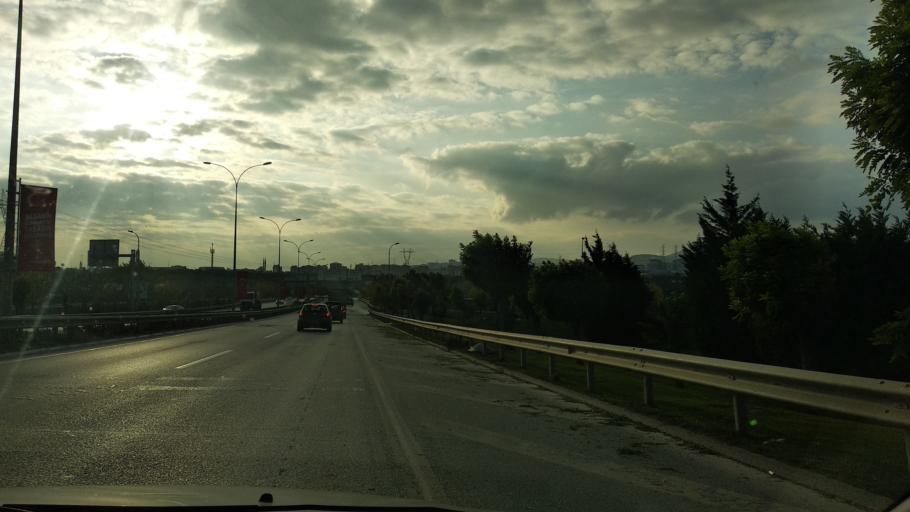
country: TR
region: Istanbul
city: Pendik
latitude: 40.9152
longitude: 29.3271
